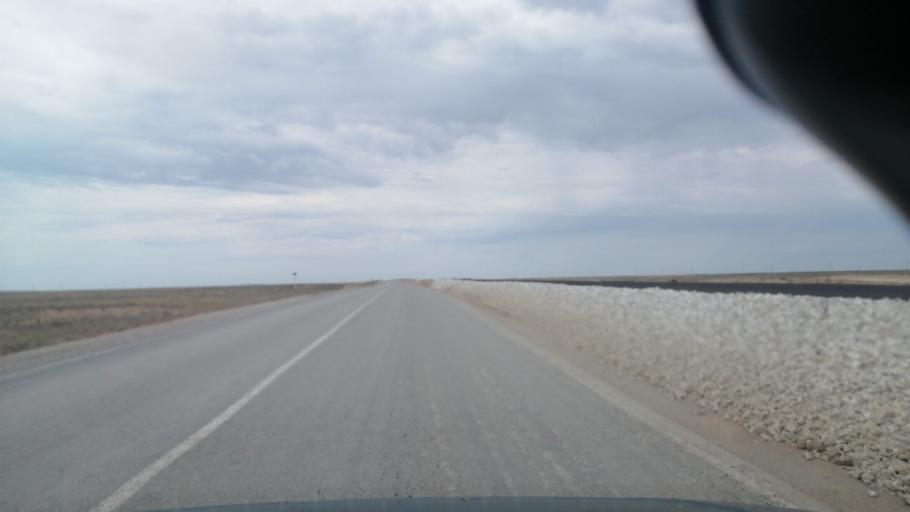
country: KZ
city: Priozersk
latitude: 46.5679
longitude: 74.2160
